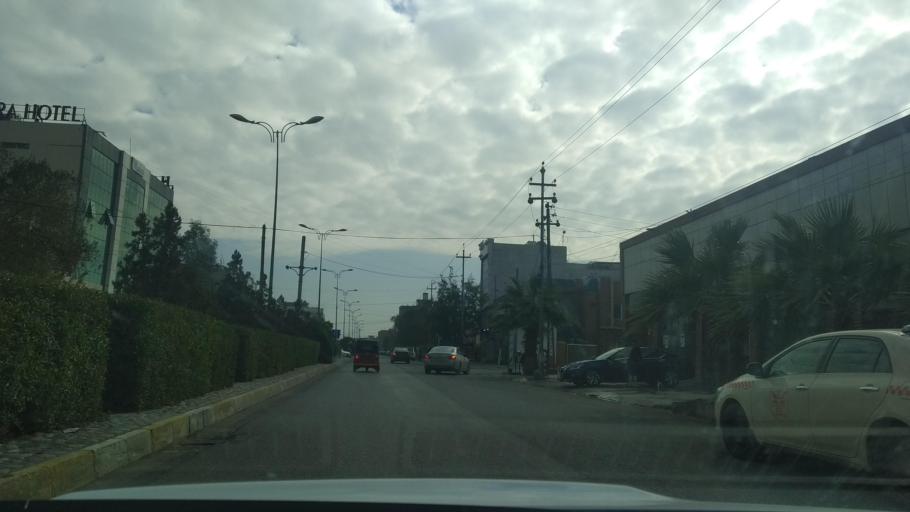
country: IQ
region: Arbil
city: Erbil
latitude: 36.1793
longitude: 44.0269
